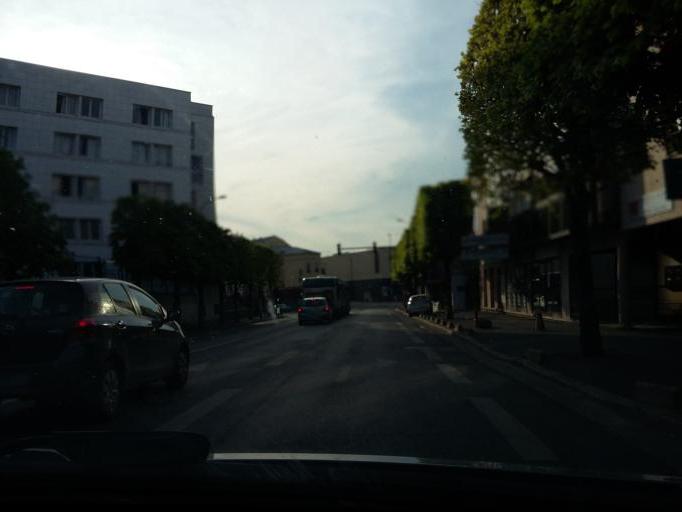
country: FR
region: Ile-de-France
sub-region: Departement du Val-d'Oise
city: Argenteuil
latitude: 48.9484
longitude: 2.2546
